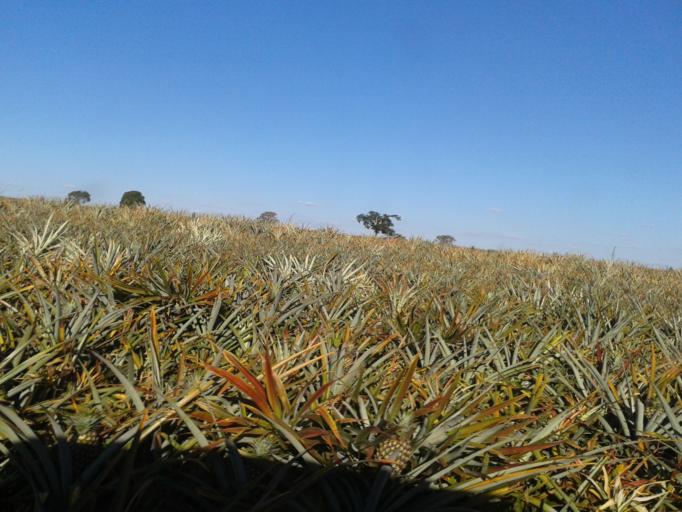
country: BR
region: Minas Gerais
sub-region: Centralina
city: Centralina
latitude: -18.7520
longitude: -49.1013
